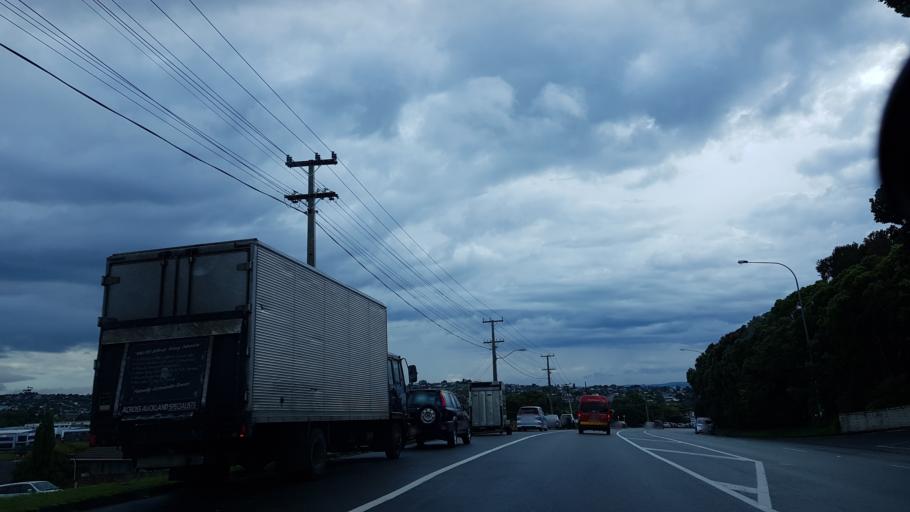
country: NZ
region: Auckland
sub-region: Auckland
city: North Shore
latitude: -36.7699
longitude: 174.7310
